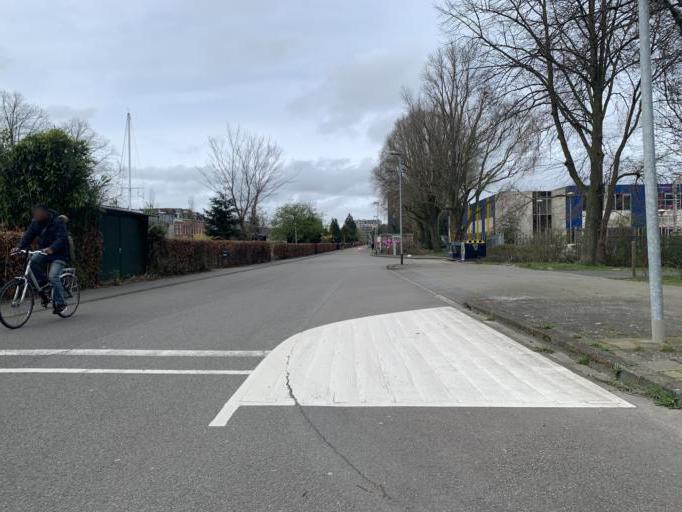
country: NL
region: Groningen
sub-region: Gemeente Groningen
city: Oosterpark
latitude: 53.2104
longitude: 6.5834
